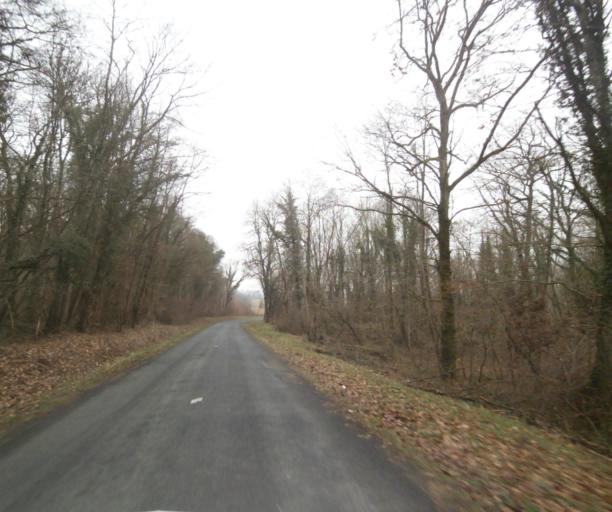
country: FR
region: Champagne-Ardenne
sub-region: Departement de la Haute-Marne
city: Bienville
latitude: 48.5704
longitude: 5.0199
